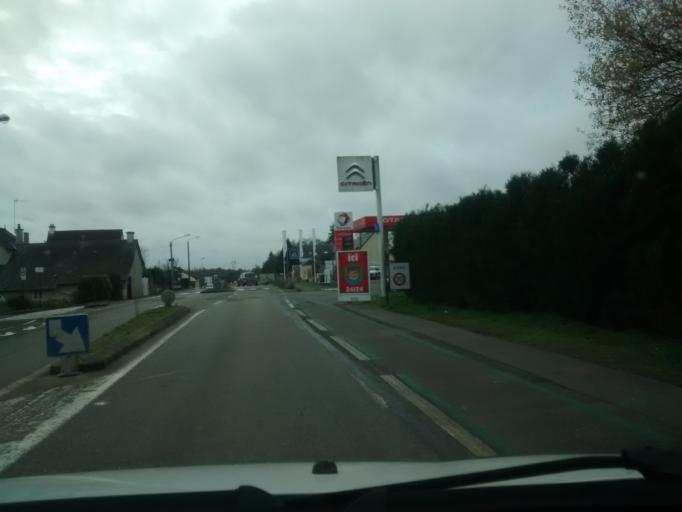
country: FR
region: Brittany
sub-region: Departement d'Ille-et-Vilaine
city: Fouillard
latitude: 48.1570
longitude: -1.5911
